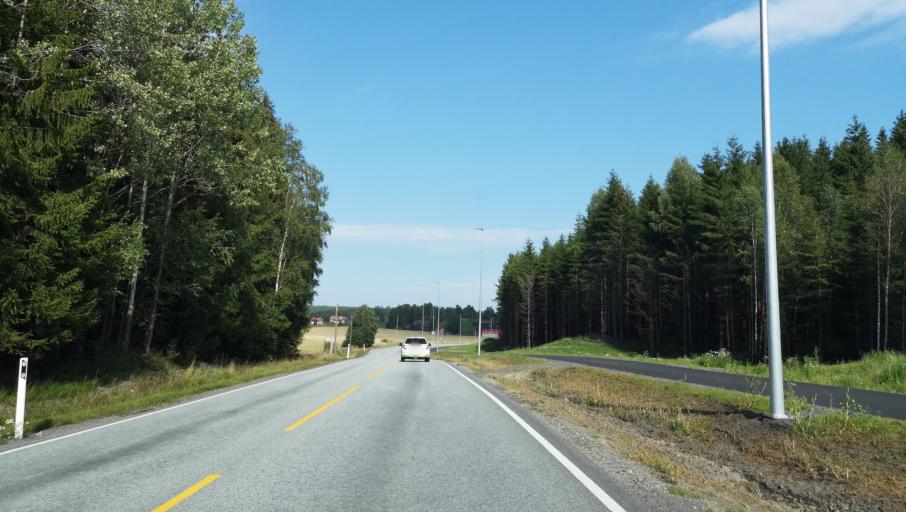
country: NO
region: Ostfold
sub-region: Valer
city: Kirkebygda
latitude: 59.4921
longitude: 10.8213
